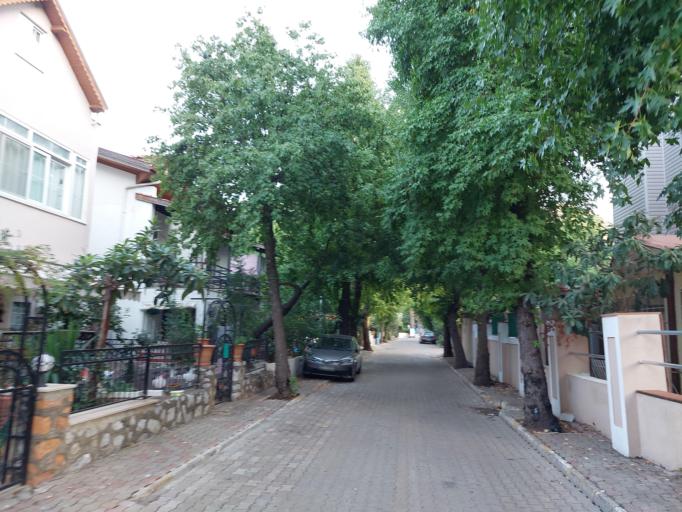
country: TR
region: Mugla
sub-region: Marmaris
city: Marmaris
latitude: 36.8019
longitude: 28.2296
